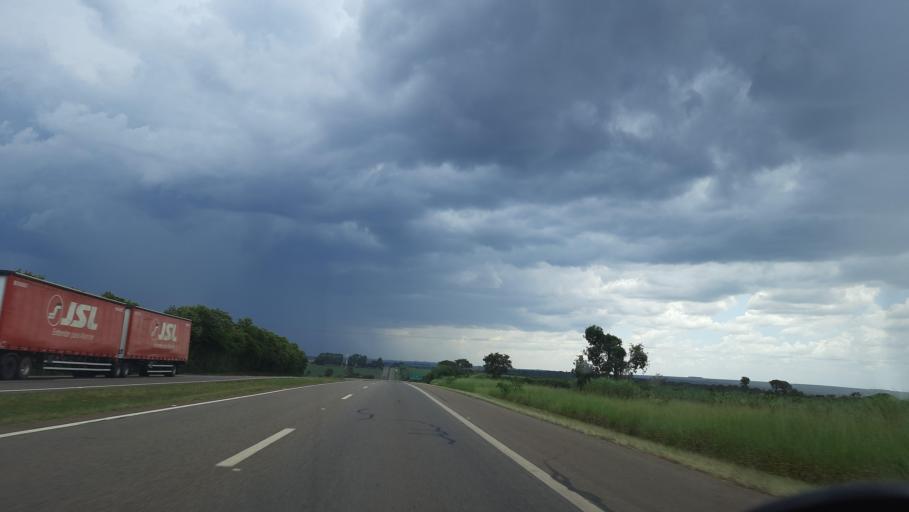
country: BR
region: Sao Paulo
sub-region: Aguai
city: Aguai
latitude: -22.0400
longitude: -47.0314
